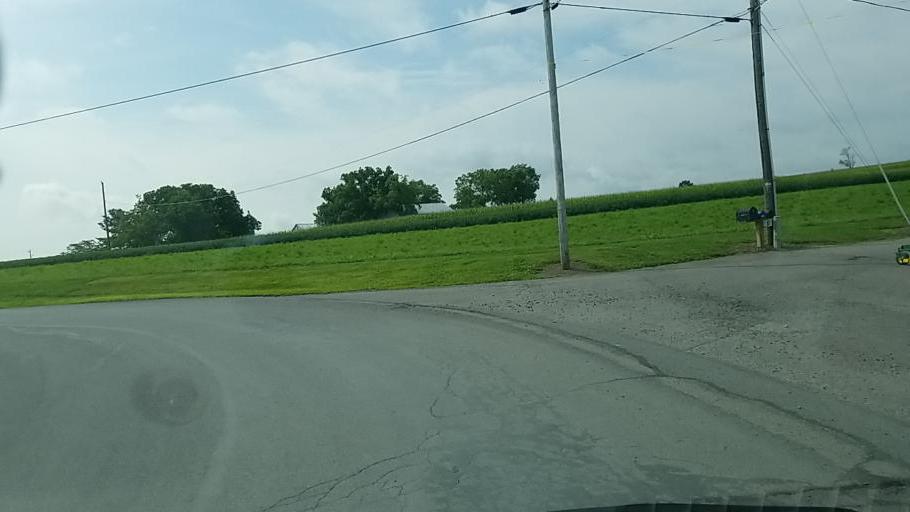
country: US
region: Pennsylvania
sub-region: Dauphin County
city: Matamoras
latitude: 40.4991
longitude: -76.8891
